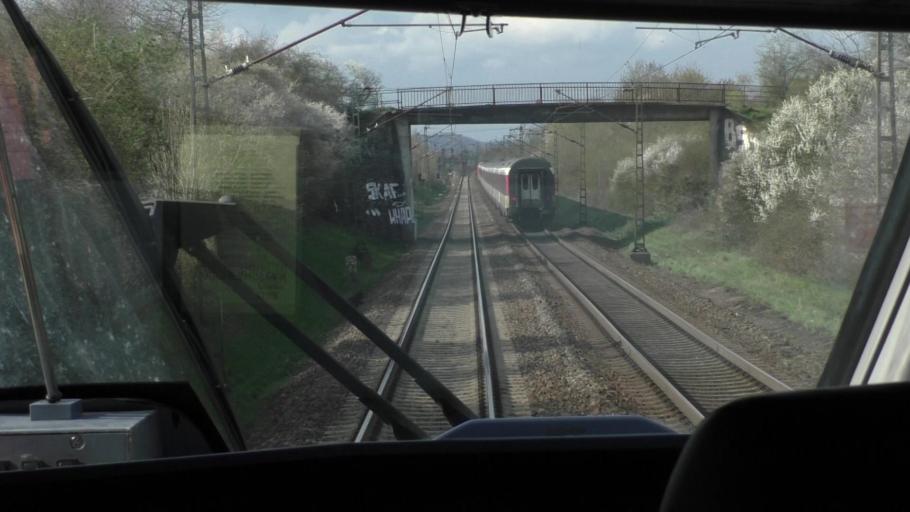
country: DE
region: Rheinland-Pfalz
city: Sinzig
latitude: 50.5595
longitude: 7.2491
